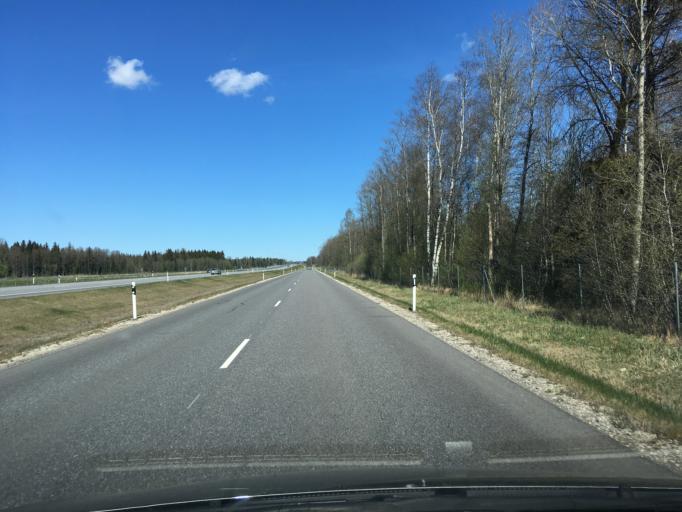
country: EE
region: Harju
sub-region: Rae vald
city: Vaida
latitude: 59.2111
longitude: 25.0384
